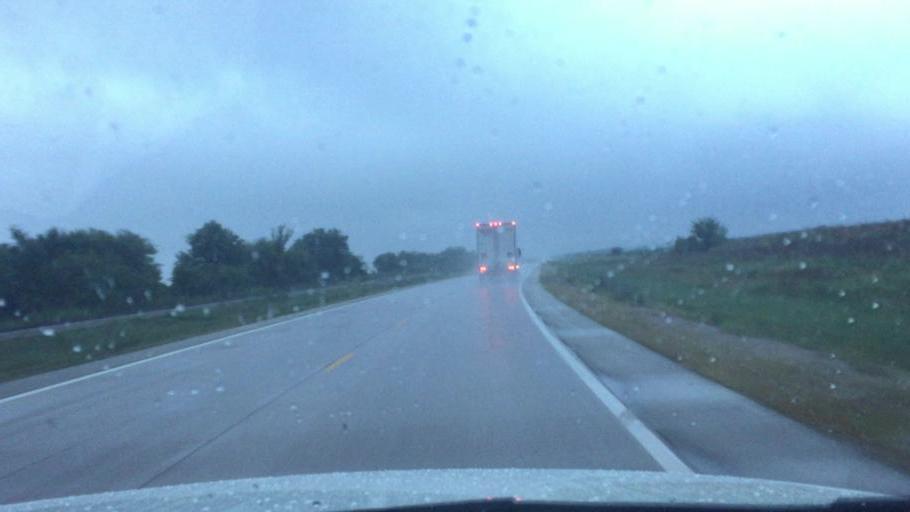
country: US
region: Kansas
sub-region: Neosho County
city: Chanute
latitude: 37.5740
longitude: -95.4710
